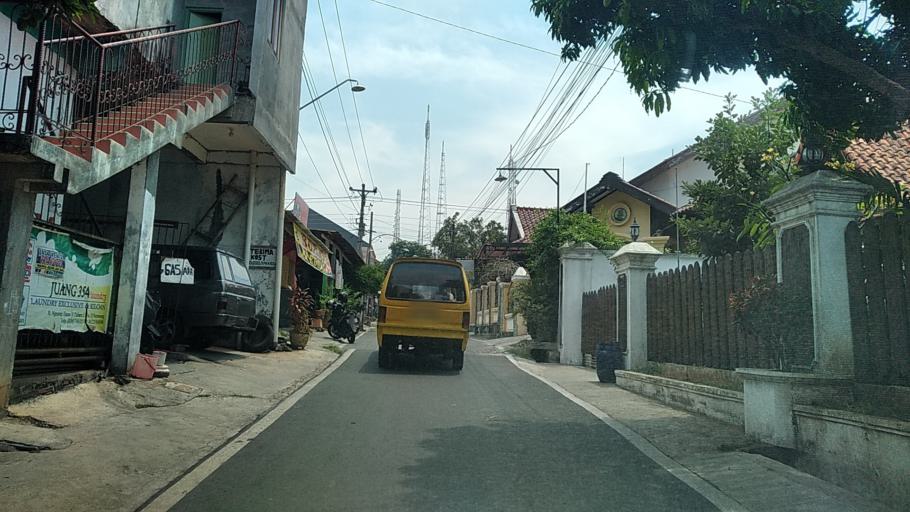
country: ID
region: Central Java
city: Semarang
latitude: -7.0484
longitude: 110.4215
